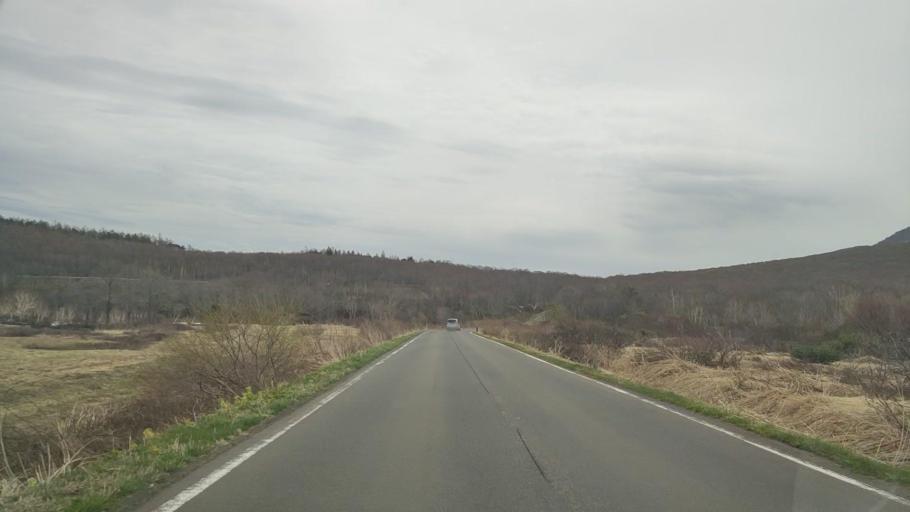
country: JP
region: Aomori
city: Aomori Shi
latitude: 40.6674
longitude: 140.9535
